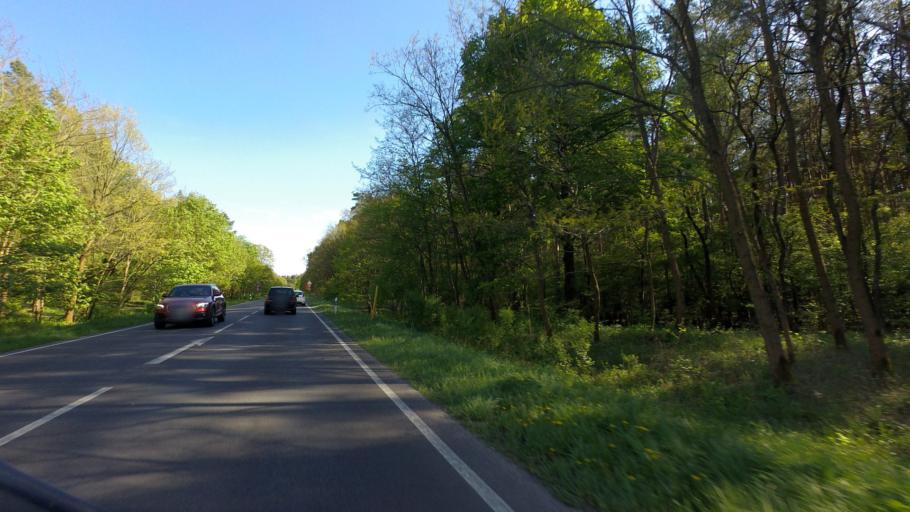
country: DE
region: Brandenburg
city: Oranienburg
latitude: 52.7164
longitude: 13.2559
